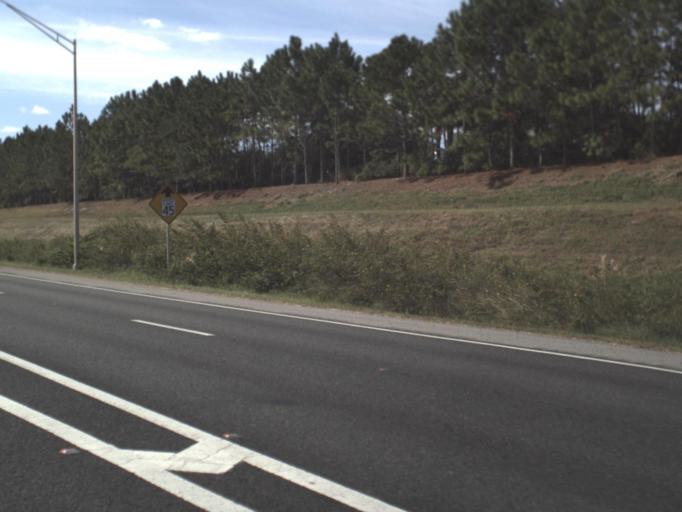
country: US
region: Florida
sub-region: Orange County
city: Gotha
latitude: 28.5391
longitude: -81.5236
